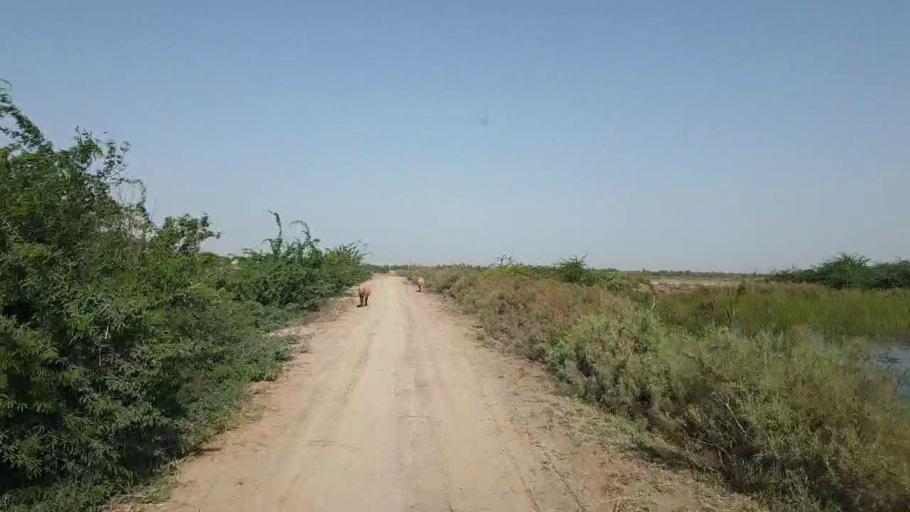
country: PK
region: Sindh
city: Tando Bago
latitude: 24.6592
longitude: 69.0693
